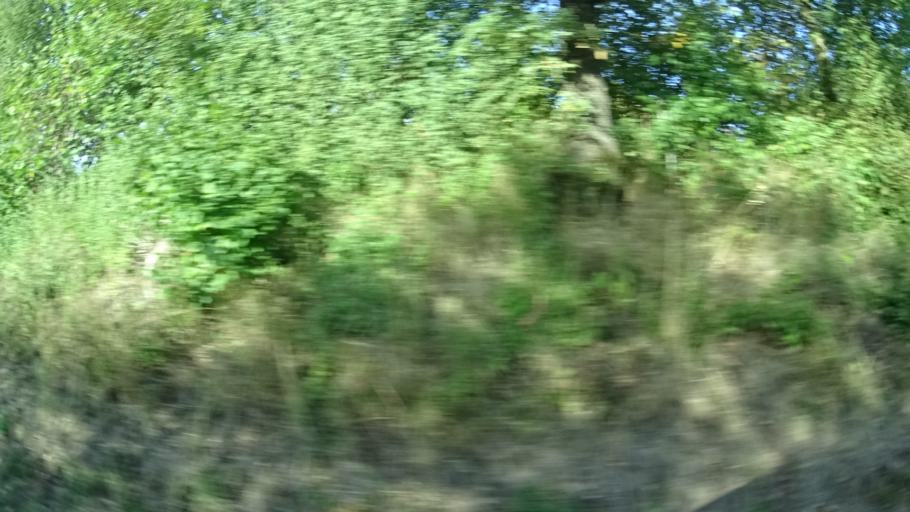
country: DE
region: Hesse
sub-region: Regierungsbezirk Giessen
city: Freiensteinau
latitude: 50.3908
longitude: 9.4403
